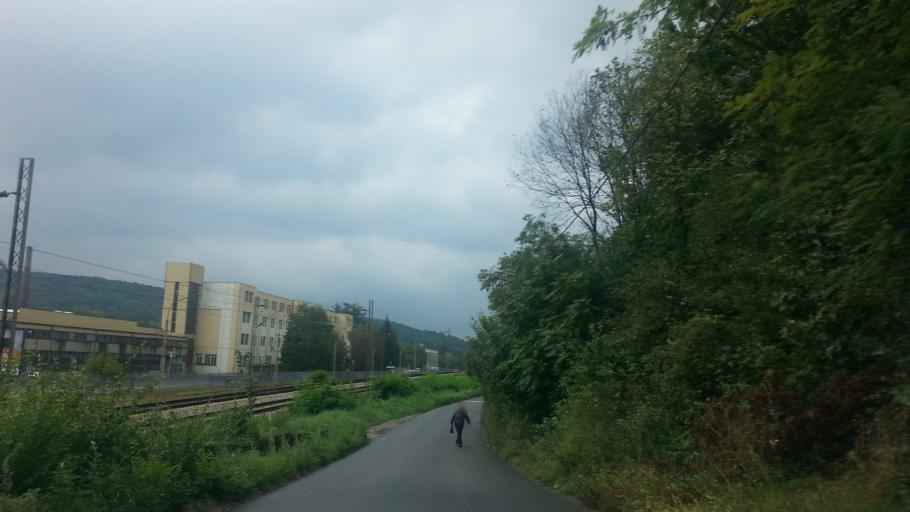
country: RS
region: Central Serbia
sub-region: Belgrade
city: Rakovica
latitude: 44.7506
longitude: 20.4455
